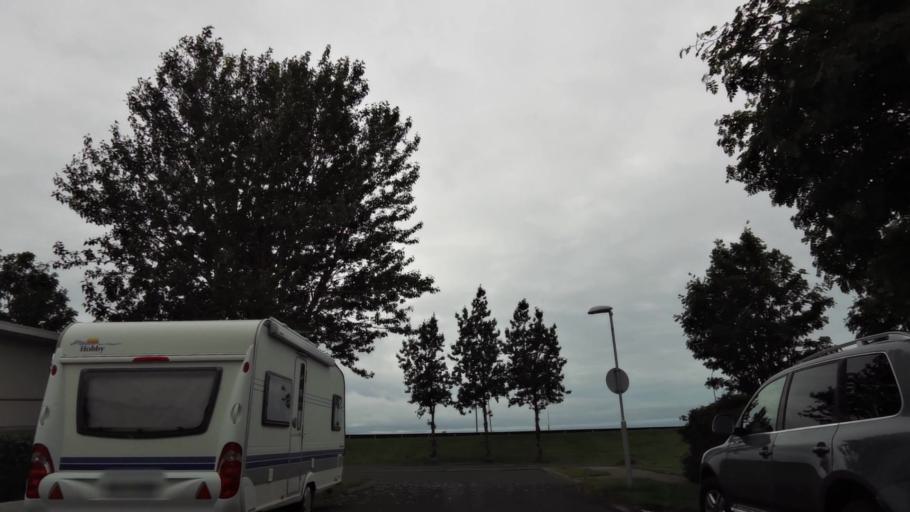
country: IS
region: Capital Region
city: Gardabaer
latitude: 64.0944
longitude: -21.9218
